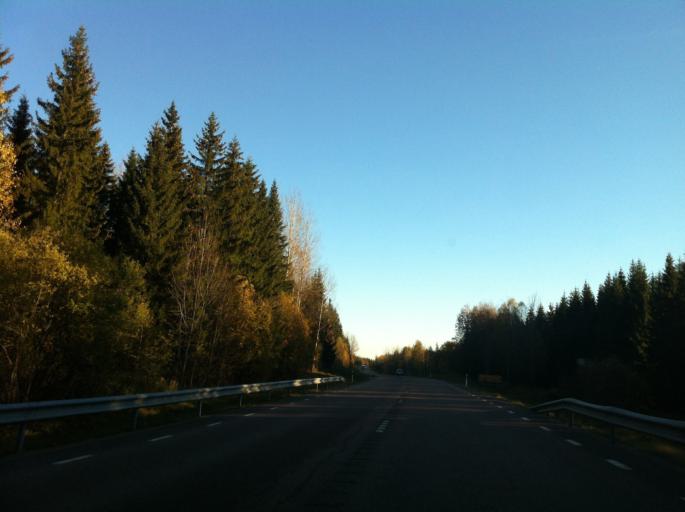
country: SE
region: Dalarna
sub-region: Faluns Kommun
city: Falun
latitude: 60.6524
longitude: 15.5585
